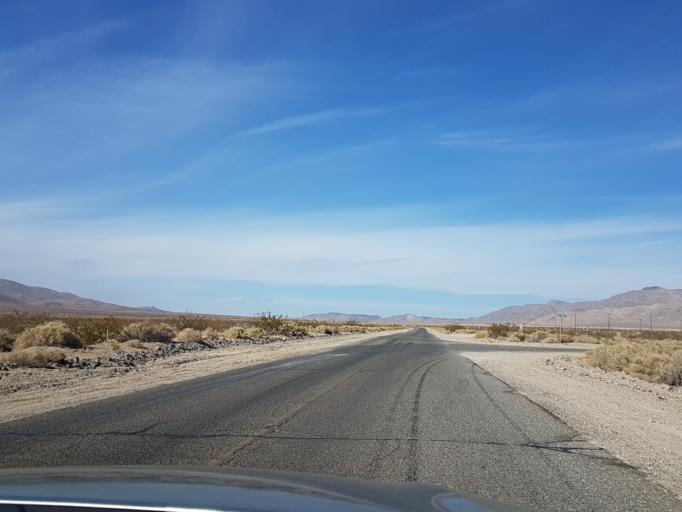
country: US
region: California
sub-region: San Bernardino County
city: Searles Valley
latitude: 35.8283
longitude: -117.3389
